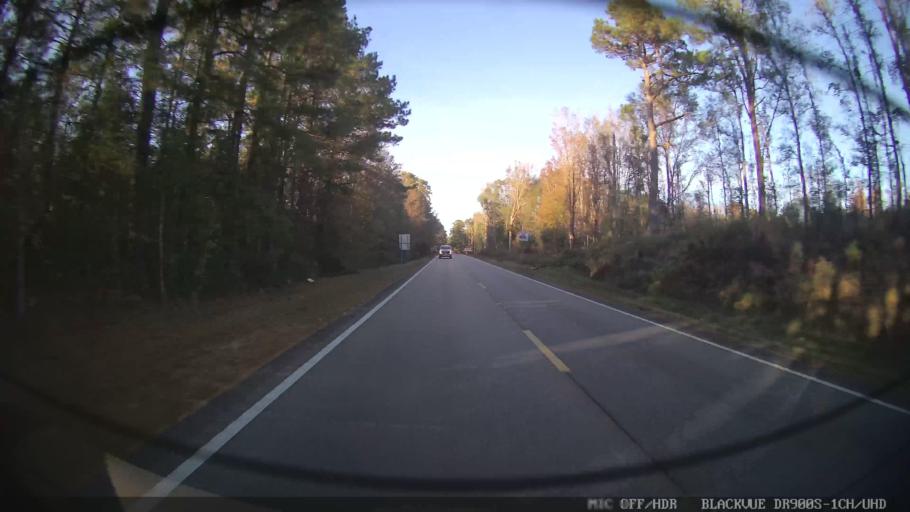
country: US
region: Mississippi
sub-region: Lamar County
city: Lumberton
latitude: 31.0150
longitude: -89.4505
